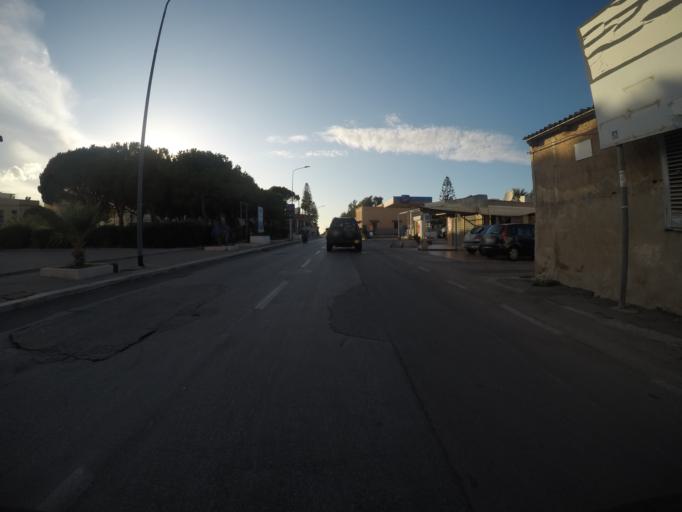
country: IT
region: Sicily
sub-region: Palermo
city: Isola delle Femmine
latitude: 38.1988
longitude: 13.2471
